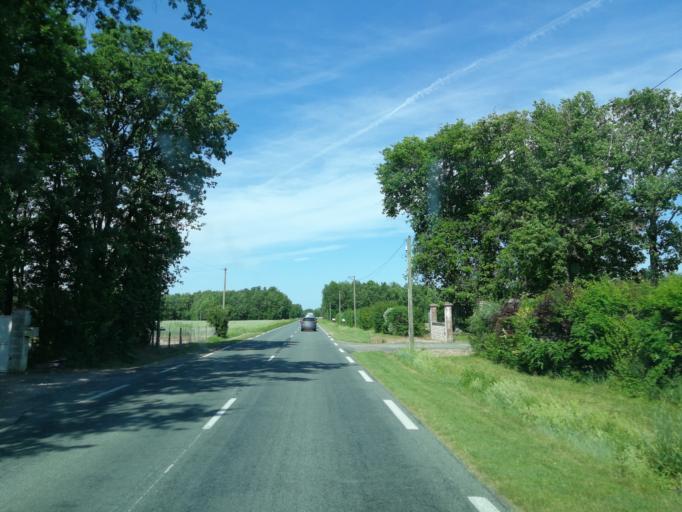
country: FR
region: Poitou-Charentes
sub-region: Departement de la Vienne
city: Loudun
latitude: 47.0532
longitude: 0.1463
